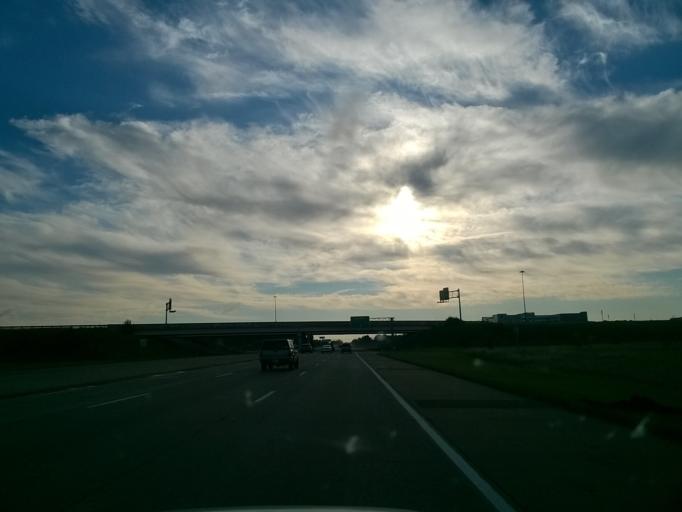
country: US
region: Indiana
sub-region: Warrick County
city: Newburgh
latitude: 37.9767
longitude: -87.4521
